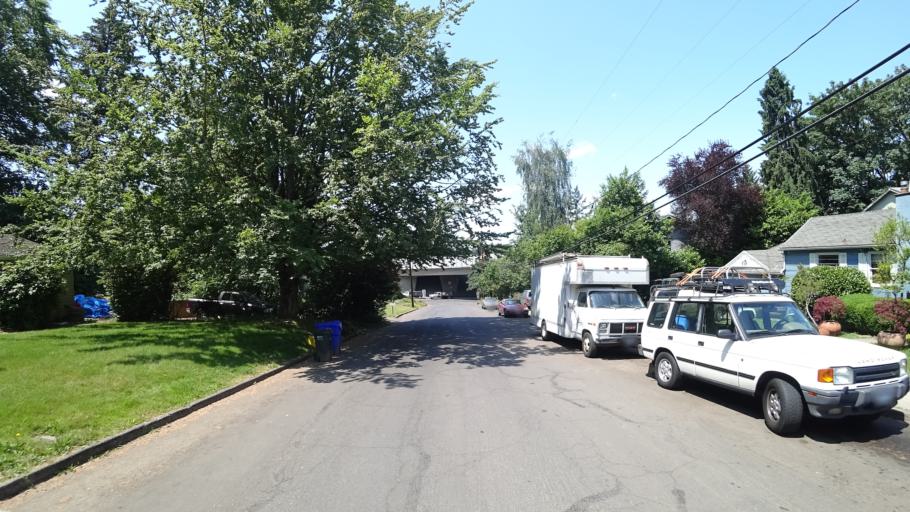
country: US
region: Oregon
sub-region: Multnomah County
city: Lents
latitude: 45.4639
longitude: -122.5675
